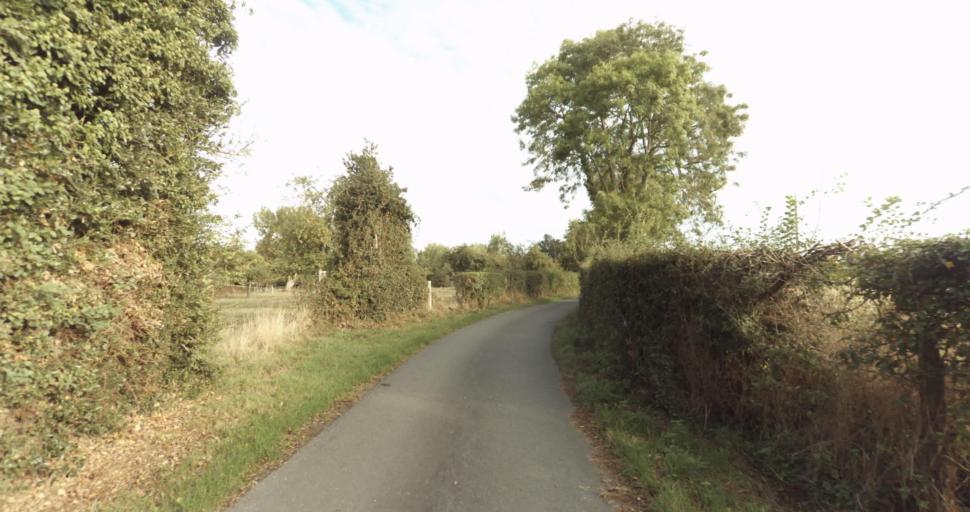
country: FR
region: Lower Normandy
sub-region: Departement de l'Orne
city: Vimoutiers
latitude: 48.8852
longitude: 0.2364
